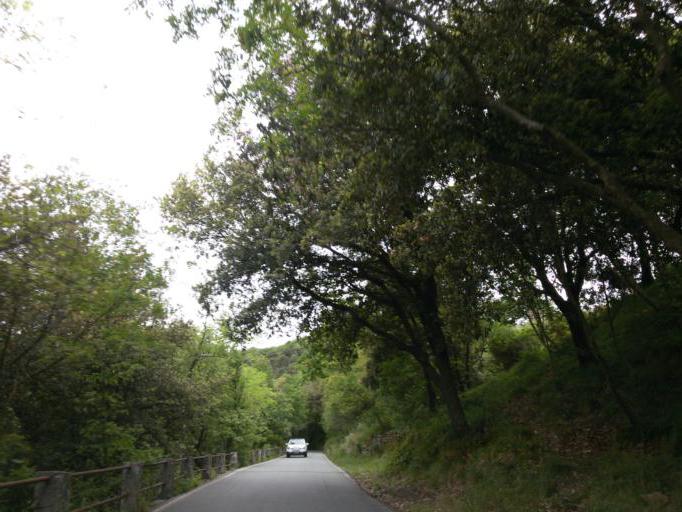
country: IT
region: Liguria
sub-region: Provincia di Genova
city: Genoa
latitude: 44.4371
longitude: 8.9316
